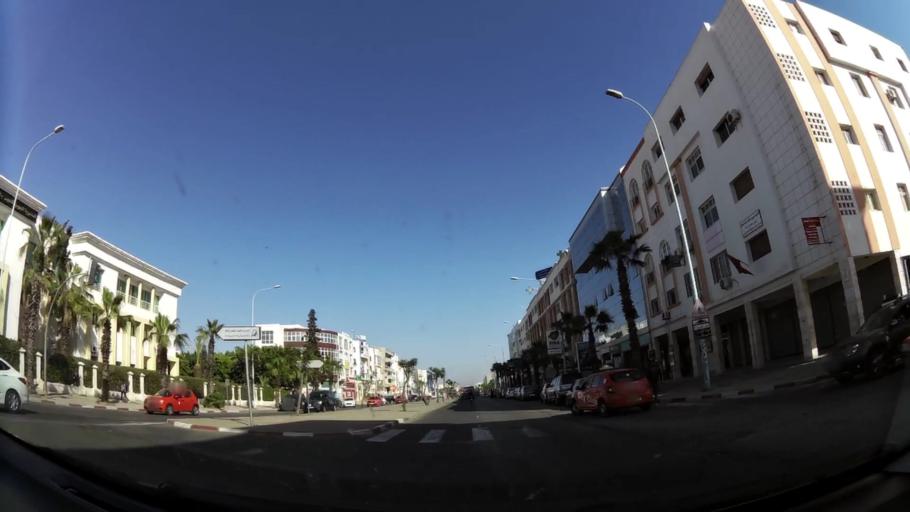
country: MA
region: Oued ed Dahab-Lagouira
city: Dakhla
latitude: 30.4123
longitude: -9.5648
